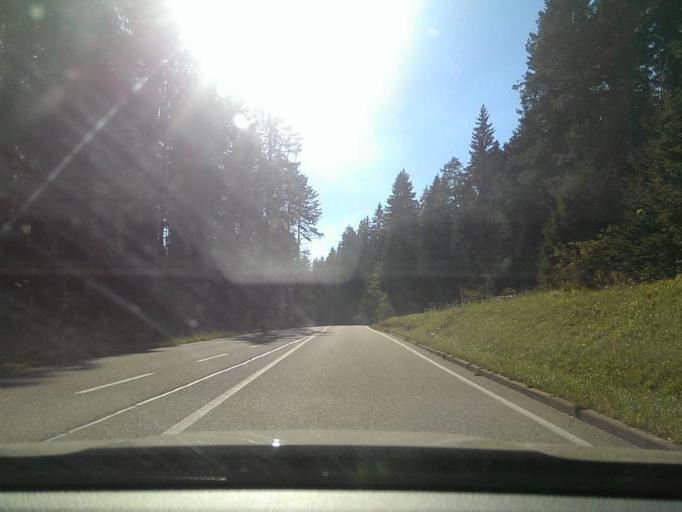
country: DE
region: Baden-Wuerttemberg
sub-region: Karlsruhe Region
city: Simmersfeld
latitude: 48.6431
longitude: 8.5080
